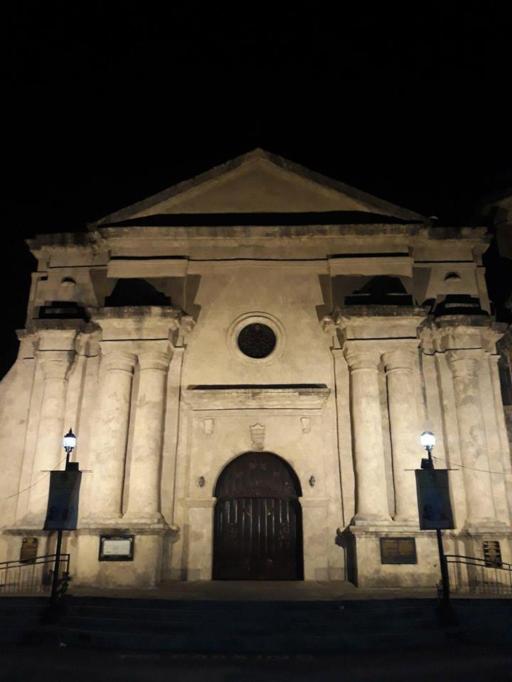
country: PH
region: Calabarzon
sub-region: Province of Batangas
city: Calaca
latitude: 13.9345
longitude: 120.8138
